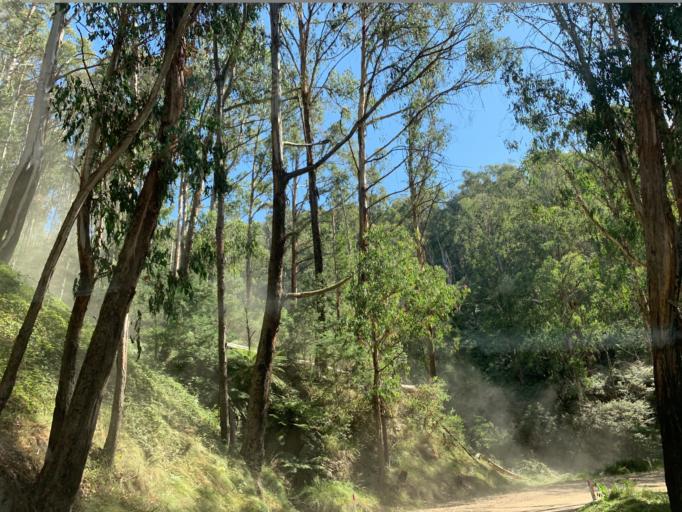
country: AU
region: Victoria
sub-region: Mansfield
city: Mansfield
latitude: -37.1008
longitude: 146.4794
